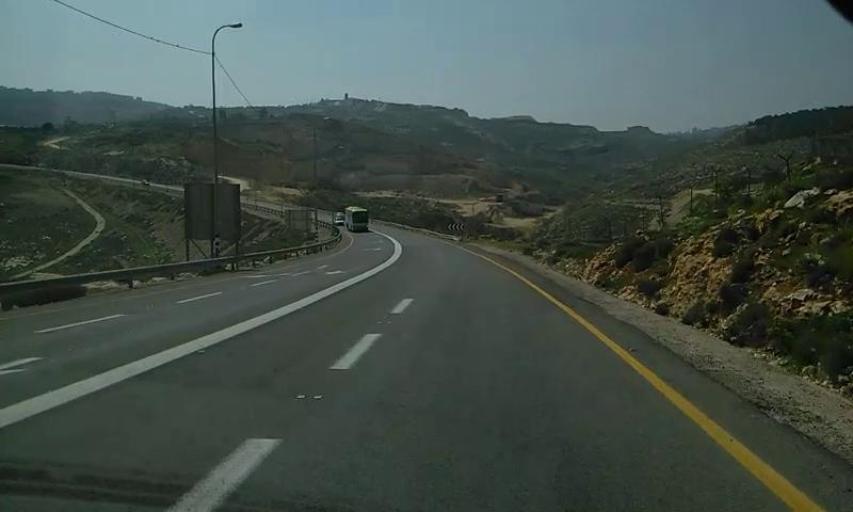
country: PS
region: West Bank
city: Jaba`
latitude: 31.8717
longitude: 35.2597
